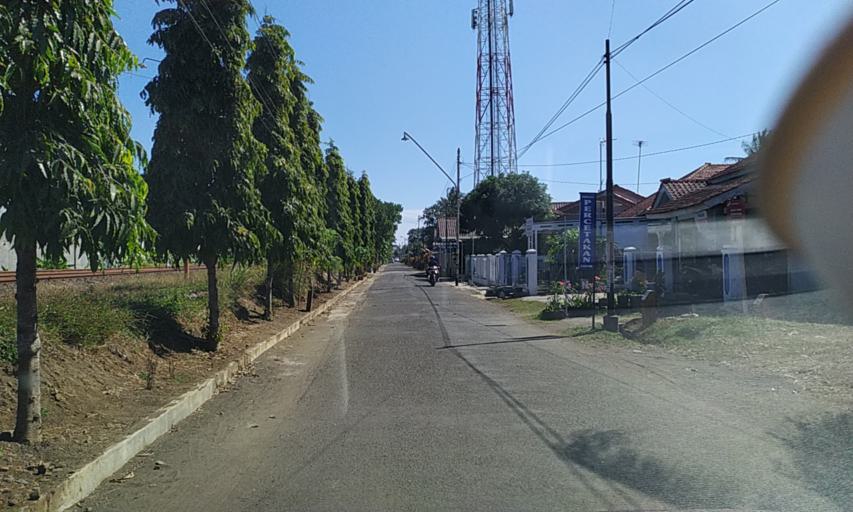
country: ID
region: Central Java
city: Rejanegara
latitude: -7.6858
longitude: 109.0411
